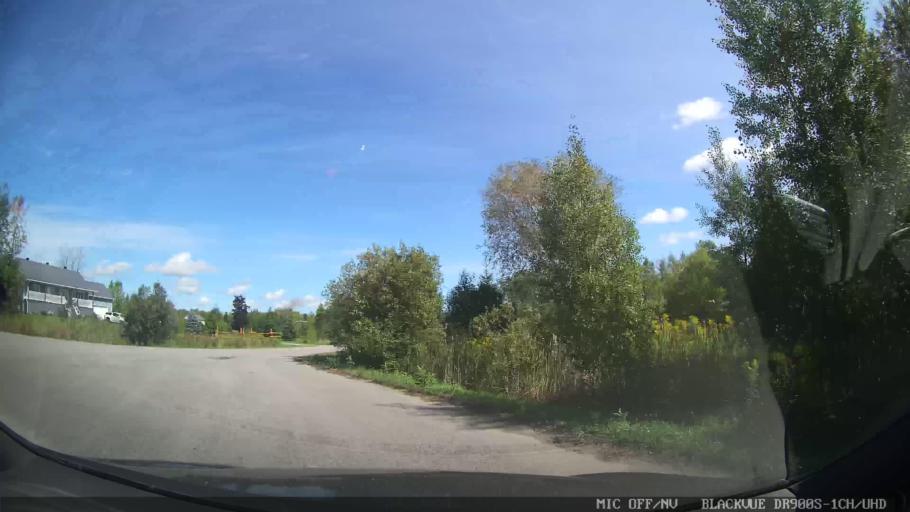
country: CA
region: Ontario
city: Bells Corners
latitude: 45.0660
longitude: -75.6660
